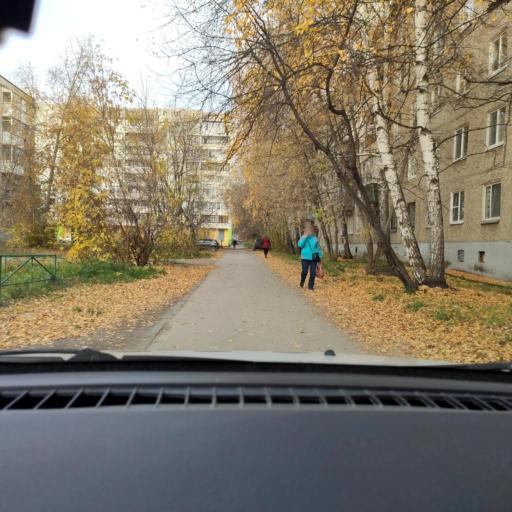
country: RU
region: Perm
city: Kondratovo
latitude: 58.0283
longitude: 56.0085
